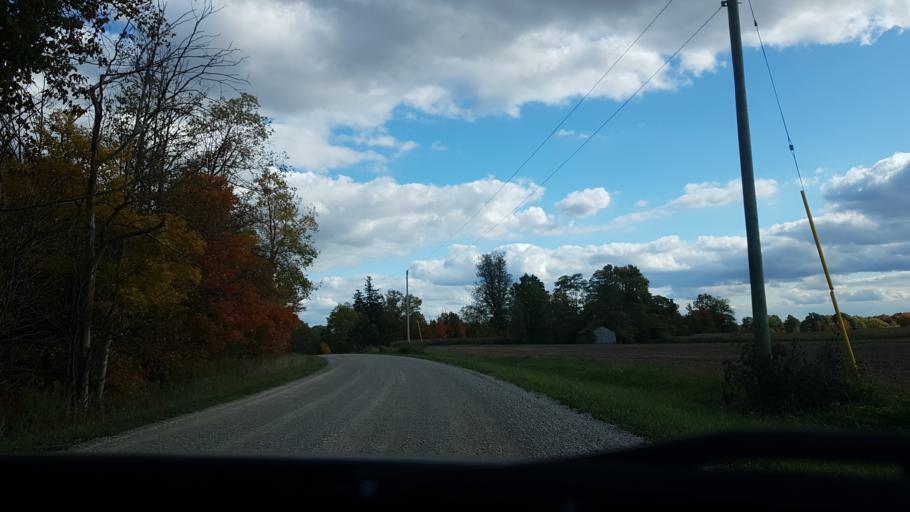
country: CA
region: Ontario
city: South Huron
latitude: 43.0970
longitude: -81.5962
